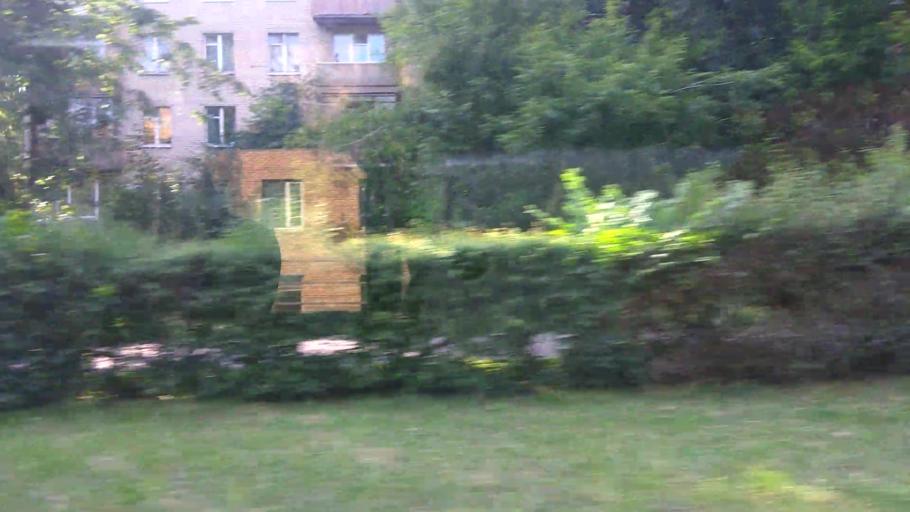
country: RU
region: Moskovskaya
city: Mytishchi
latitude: 55.9141
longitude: 37.7430
